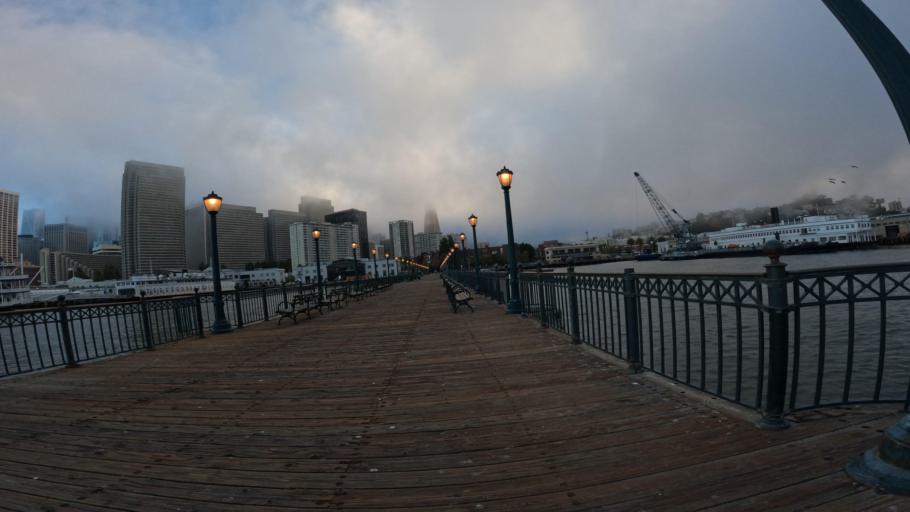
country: US
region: California
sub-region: San Francisco County
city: San Francisco
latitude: 37.8001
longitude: -122.3949
